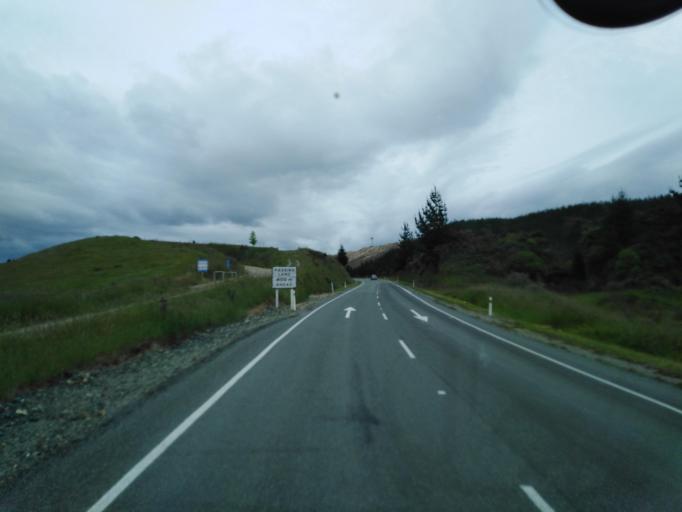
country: NZ
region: Tasman
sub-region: Tasman District
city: Wakefield
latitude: -41.4620
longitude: 172.9509
